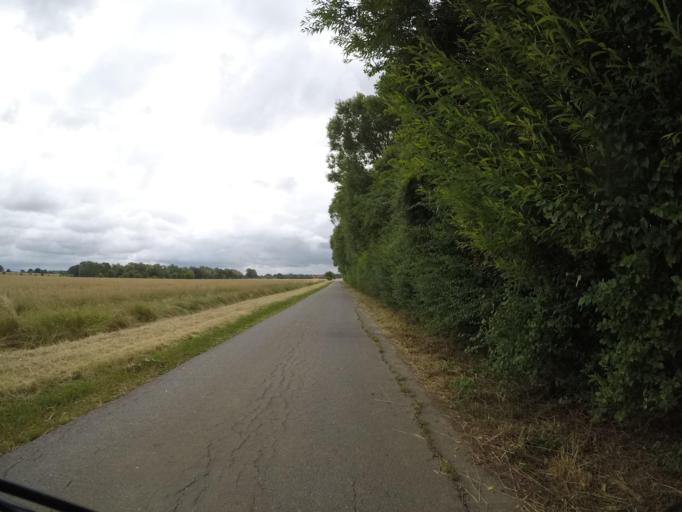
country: DE
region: Lower Saxony
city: Damnatz
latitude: 53.1735
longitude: 11.1207
